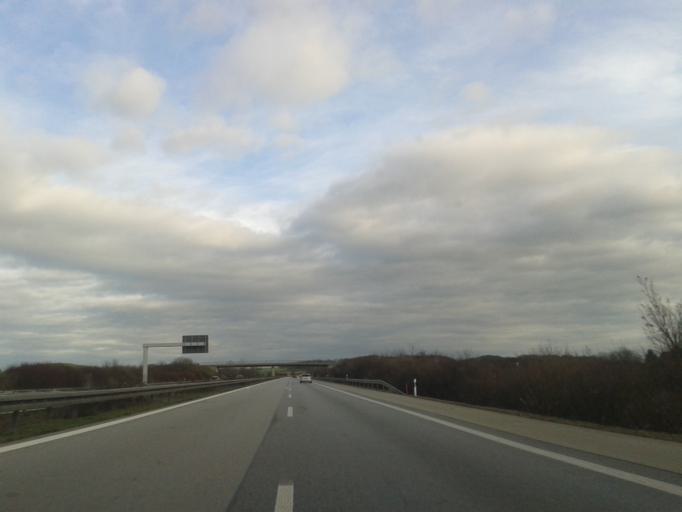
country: DE
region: Saxony
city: Kubschutz
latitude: 51.2003
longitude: 14.4780
